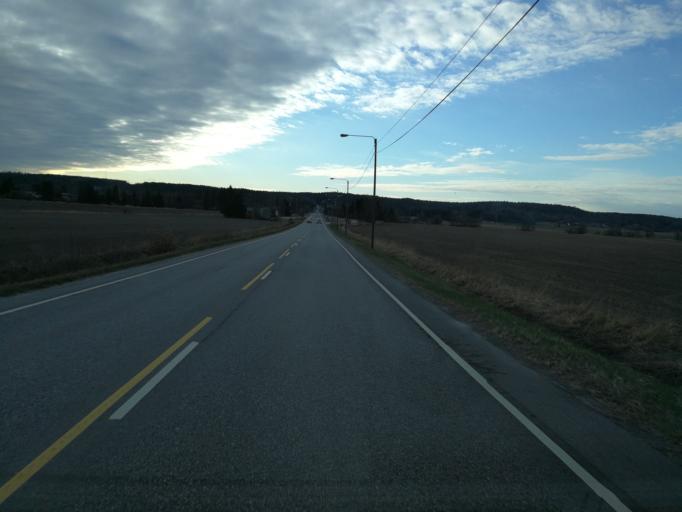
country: FI
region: Varsinais-Suomi
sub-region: Turku
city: Paimio
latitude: 60.4229
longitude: 22.6459
